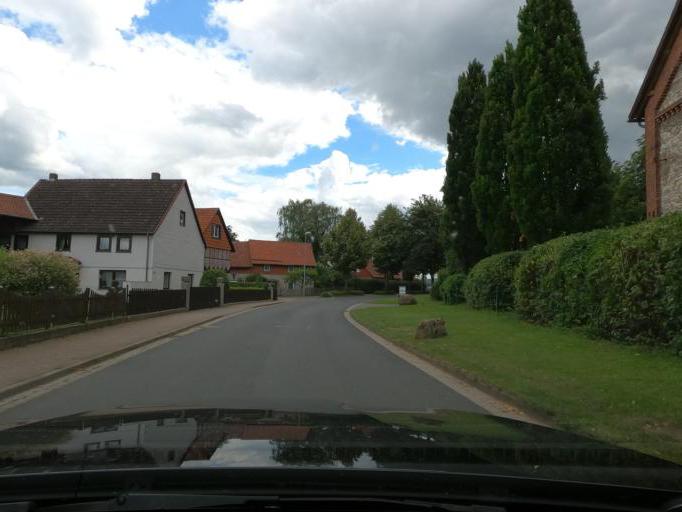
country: DE
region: Lower Saxony
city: Heere
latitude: 52.0627
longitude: 10.2508
